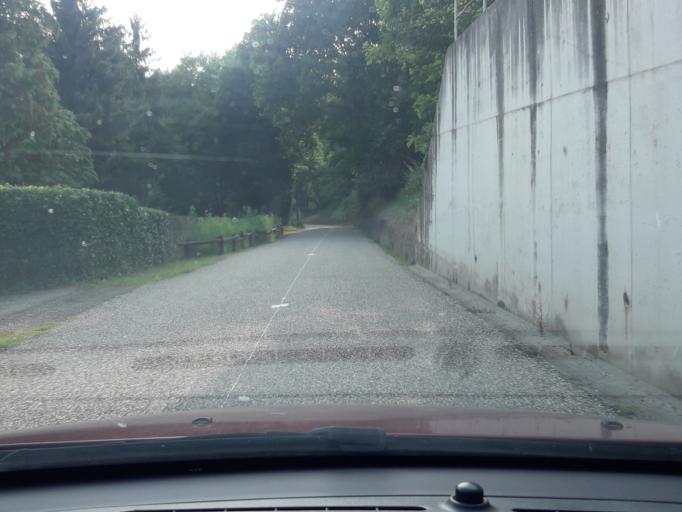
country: FR
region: Alsace
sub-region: Departement du Bas-Rhin
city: Still
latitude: 48.5370
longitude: 7.3880
